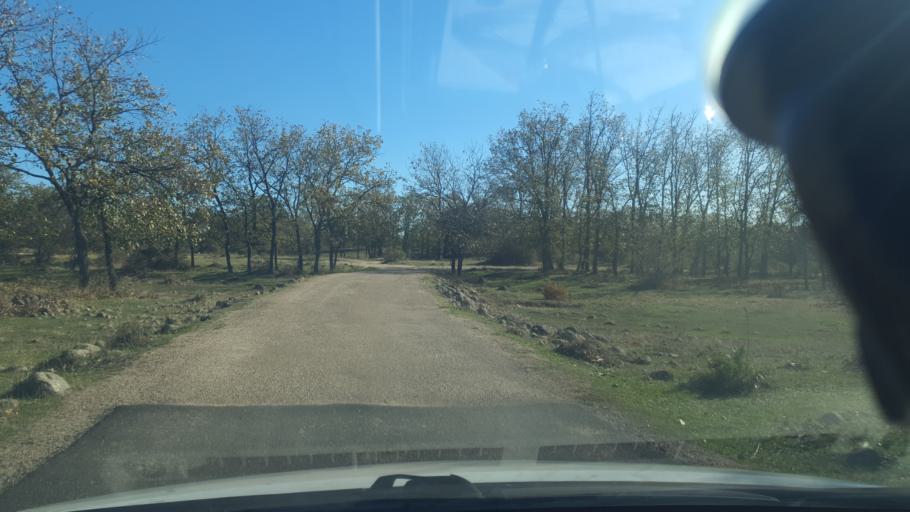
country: ES
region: Castille and Leon
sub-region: Provincia de Avila
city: Candeleda
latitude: 40.1177
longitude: -5.2600
